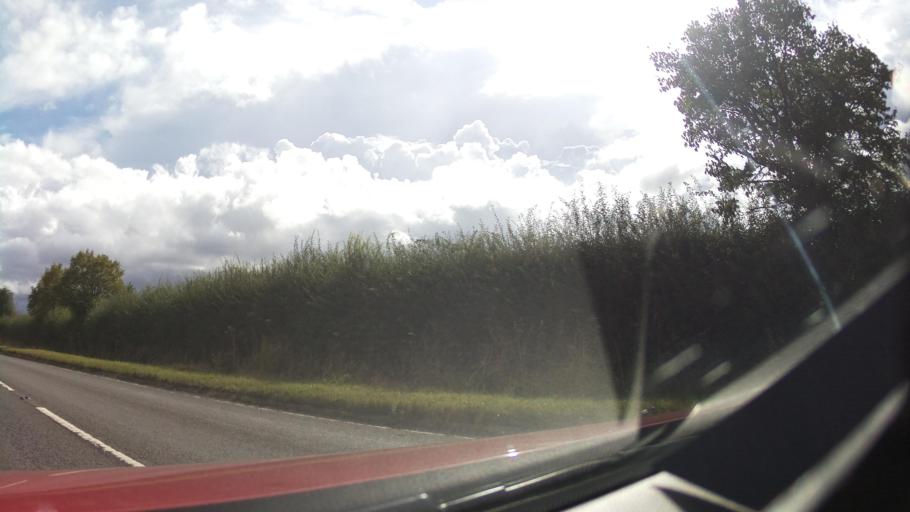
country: GB
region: England
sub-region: Telford and Wrekin
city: Madeley
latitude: 52.6157
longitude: -2.4126
